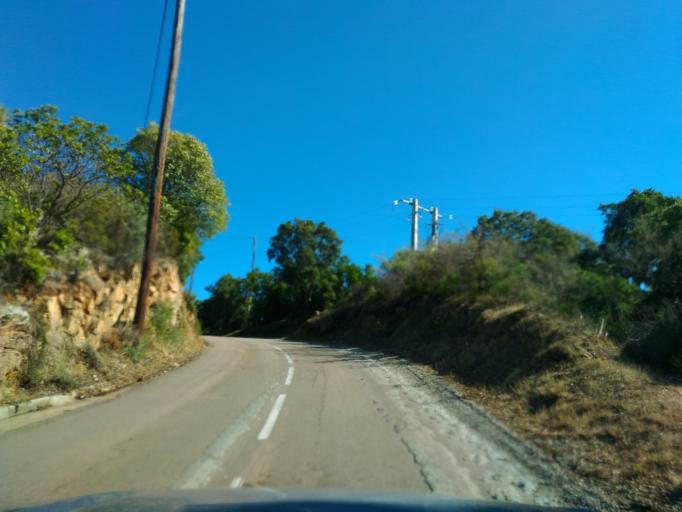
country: FR
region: Corsica
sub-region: Departement de la Corse-du-Sud
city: Sari-Solenzara
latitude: 41.6966
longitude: 9.3814
